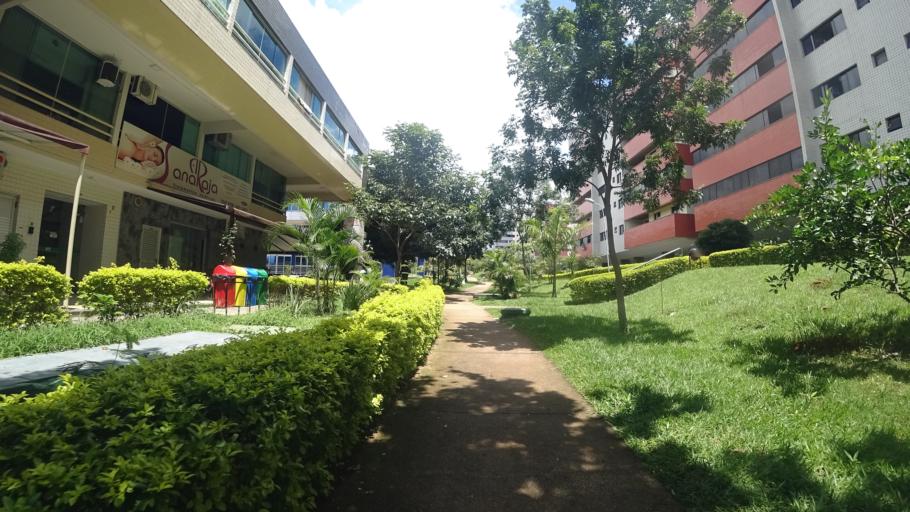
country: BR
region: Federal District
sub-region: Brasilia
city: Brasilia
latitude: -15.7445
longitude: -47.8869
